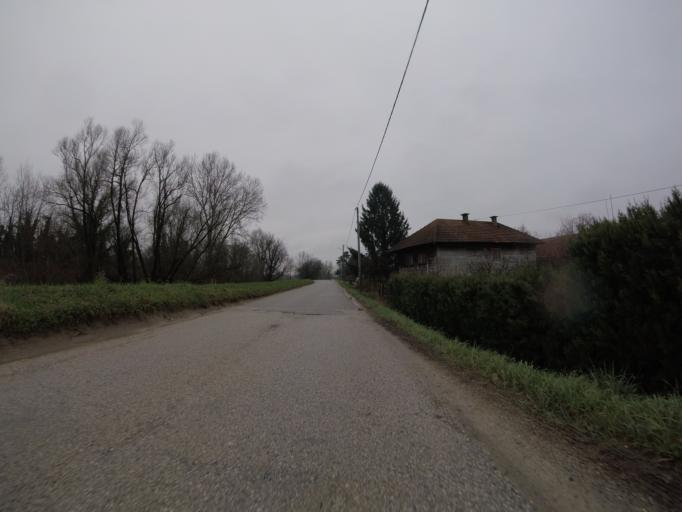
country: HR
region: Sisacko-Moslavacka
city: Lekenik
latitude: 45.6732
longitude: 16.2449
